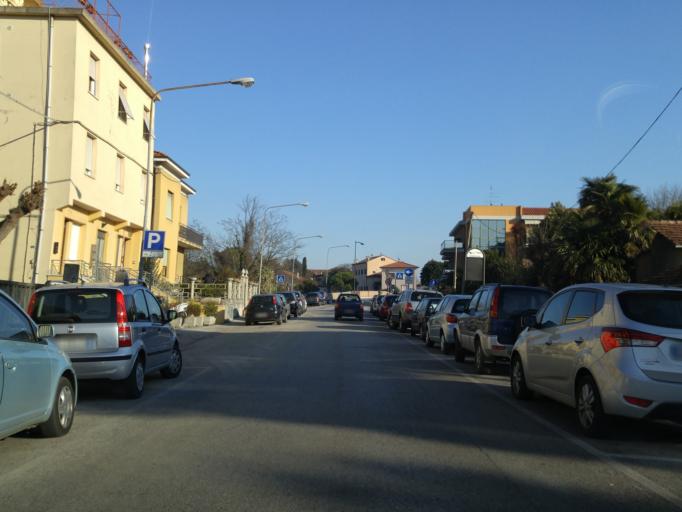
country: IT
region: The Marches
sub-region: Provincia di Pesaro e Urbino
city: Pesaro
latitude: 43.9108
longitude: 12.9008
